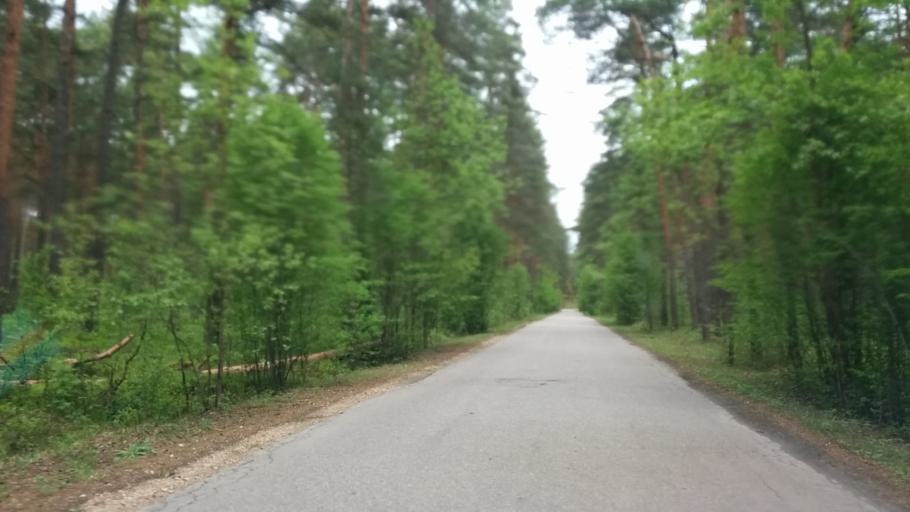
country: LV
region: Babite
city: Pinki
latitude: 56.9378
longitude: 23.9340
